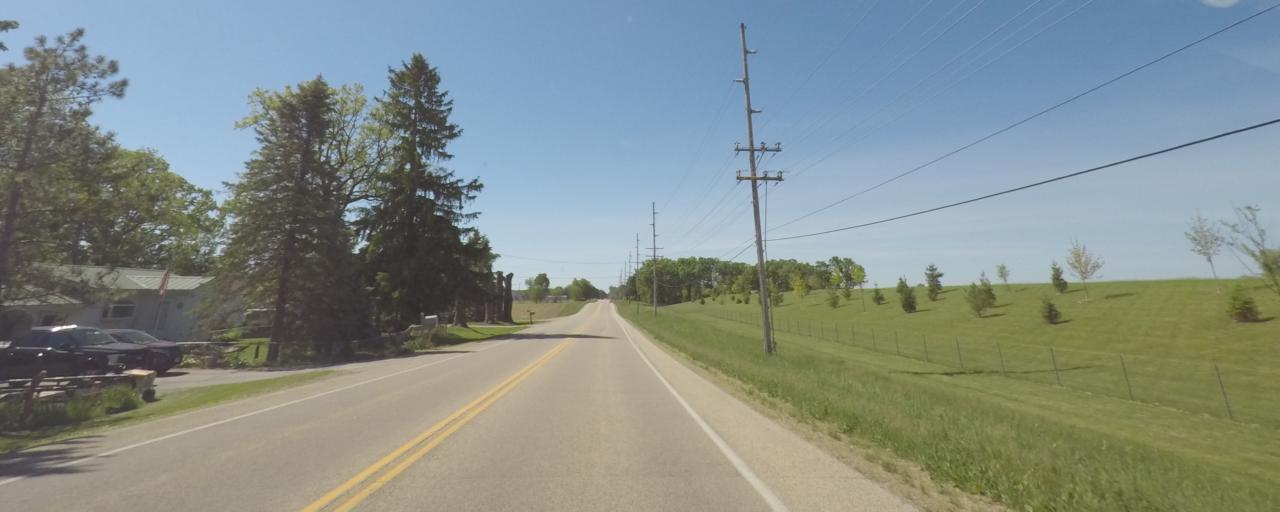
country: US
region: Wisconsin
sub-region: Green County
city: Brooklyn
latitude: 42.8678
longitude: -89.3691
